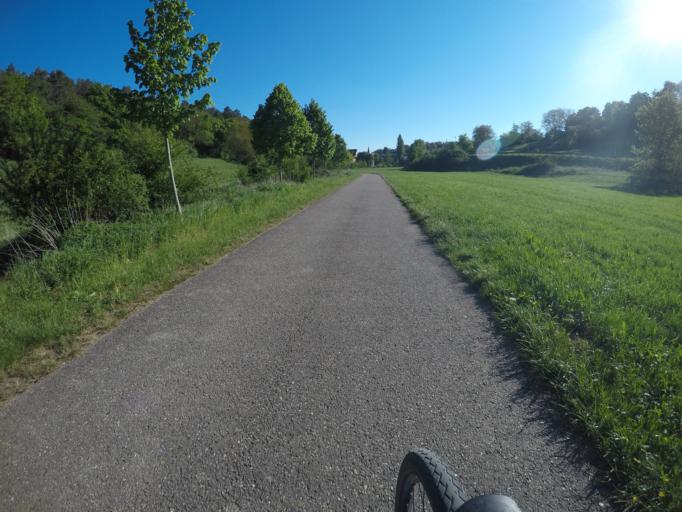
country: DE
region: Baden-Wuerttemberg
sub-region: Regierungsbezirk Stuttgart
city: Weissach
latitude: 48.8390
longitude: 8.9168
